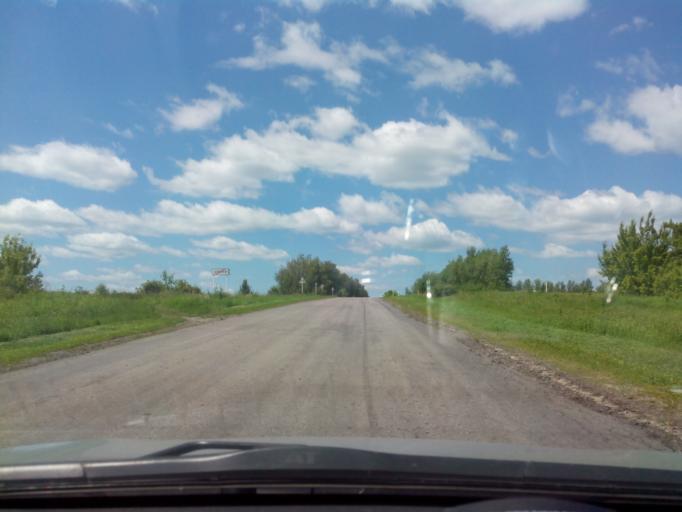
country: RU
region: Voronezj
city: Ternovka
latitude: 51.6269
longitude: 41.7566
